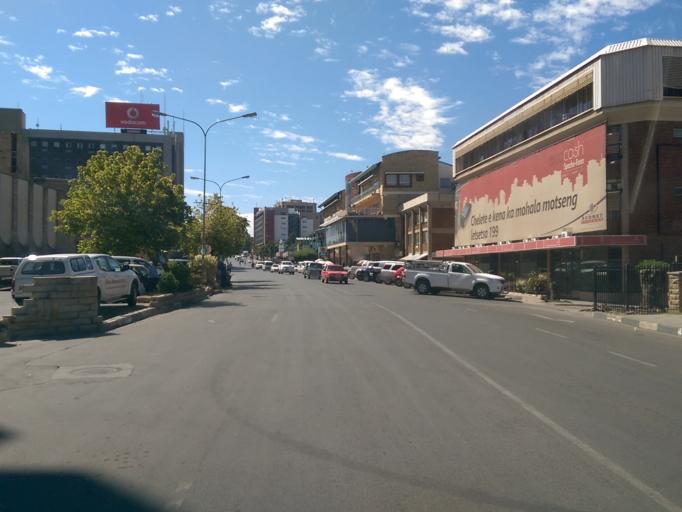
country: LS
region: Maseru
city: Maseru
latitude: -29.3128
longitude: 27.4785
